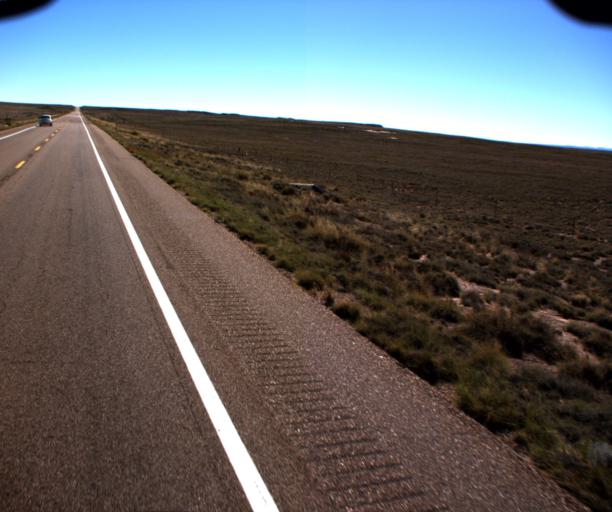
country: US
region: Arizona
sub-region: Navajo County
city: Holbrook
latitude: 34.7844
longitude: -109.8647
